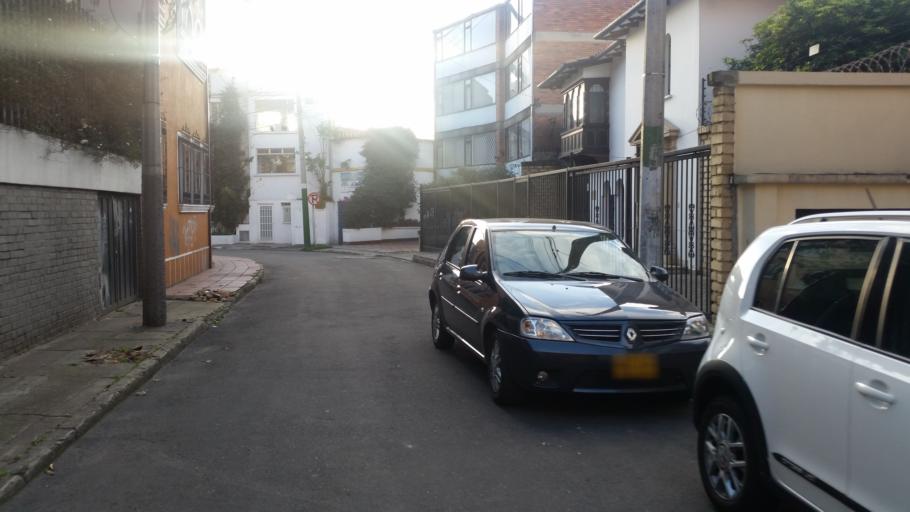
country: CO
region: Bogota D.C.
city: Bogota
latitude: 4.6211
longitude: -74.0690
